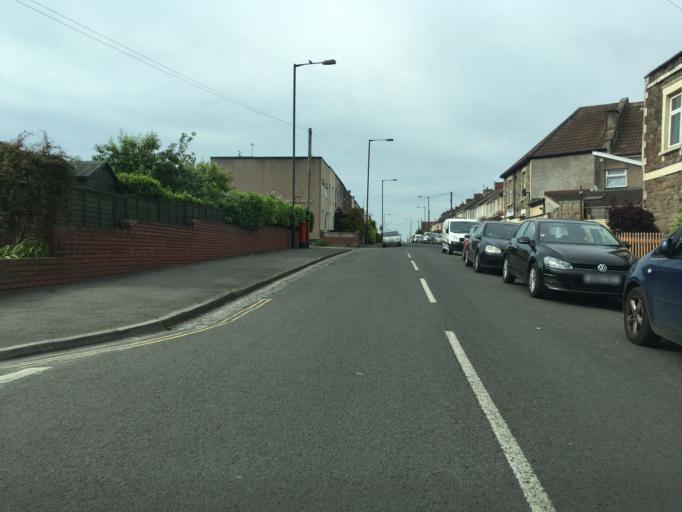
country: GB
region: England
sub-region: South Gloucestershire
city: Mangotsfield
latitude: 51.4755
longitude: -2.5247
